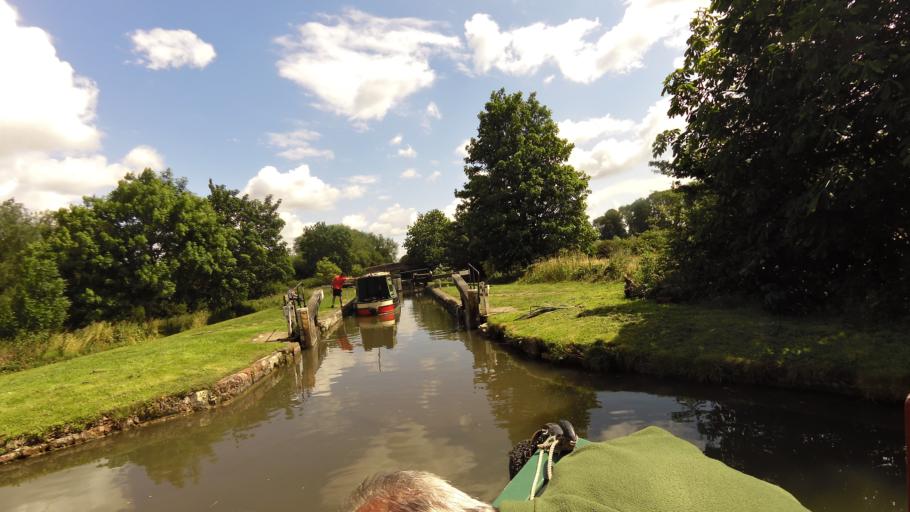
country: GB
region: England
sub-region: West Berkshire
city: Newbury
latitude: 51.3964
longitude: -1.3704
